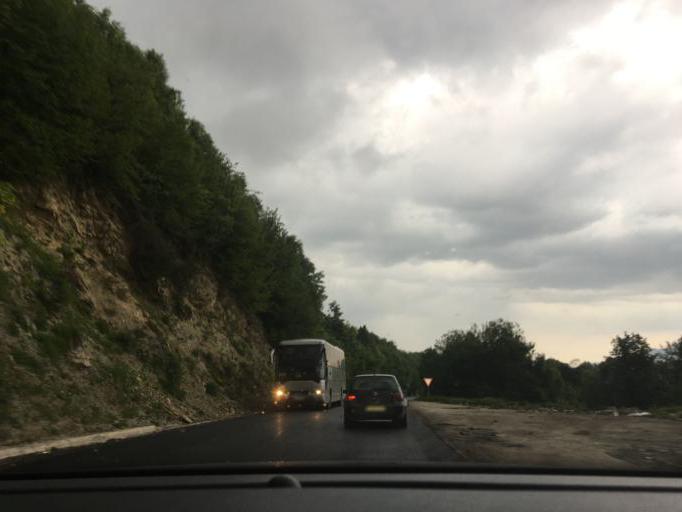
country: MK
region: Gostivar
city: Vrutok
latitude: 41.6764
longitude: 20.8485
